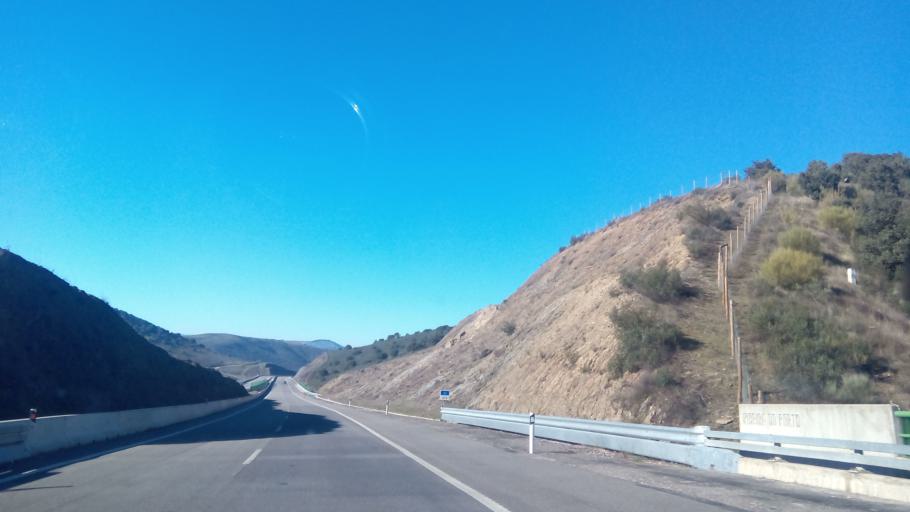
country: PT
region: Braganca
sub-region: Braganca Municipality
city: Braganca
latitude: 41.7691
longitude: -6.6614
